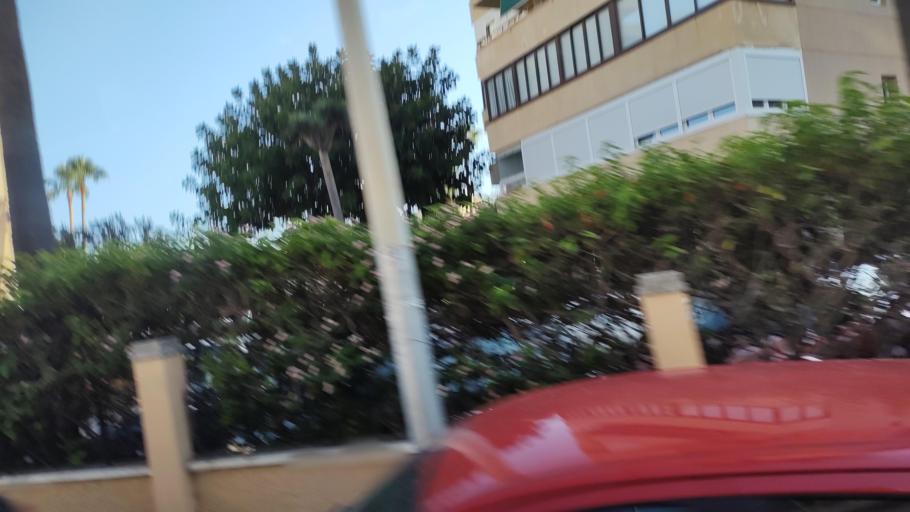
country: ES
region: Andalusia
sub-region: Provincia de Malaga
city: Torremolinos
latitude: 36.6300
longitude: -4.4910
